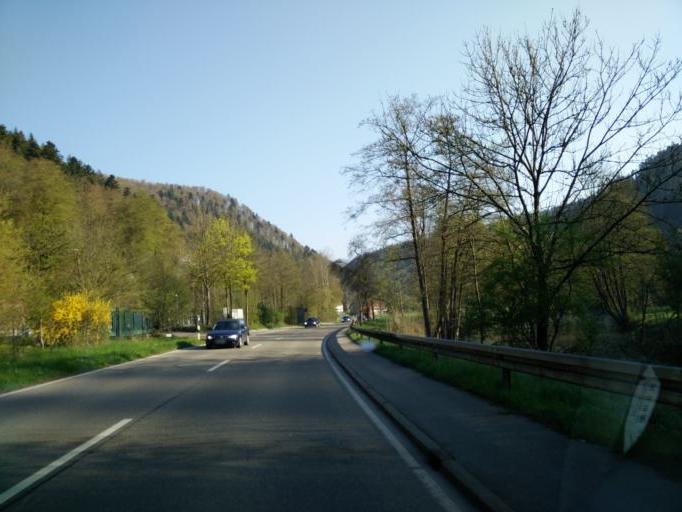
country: DE
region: Baden-Wuerttemberg
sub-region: Karlsruhe Region
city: Bad Liebenzell
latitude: 48.7452
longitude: 8.7304
